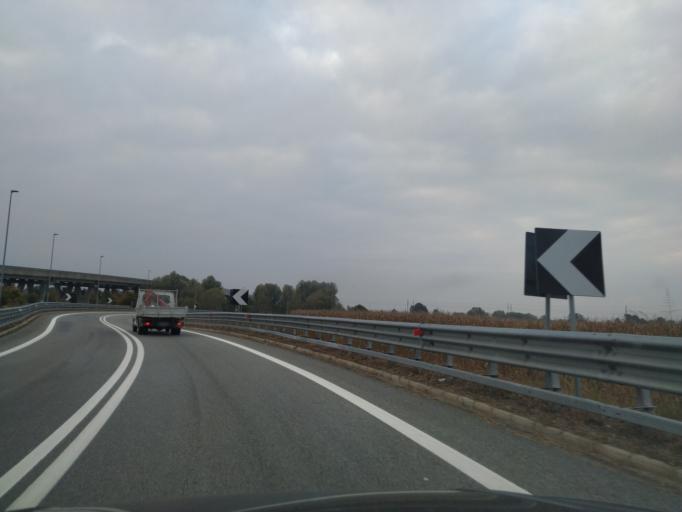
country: IT
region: Piedmont
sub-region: Provincia di Torino
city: Brandizzo
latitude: 45.1903
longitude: 7.8548
